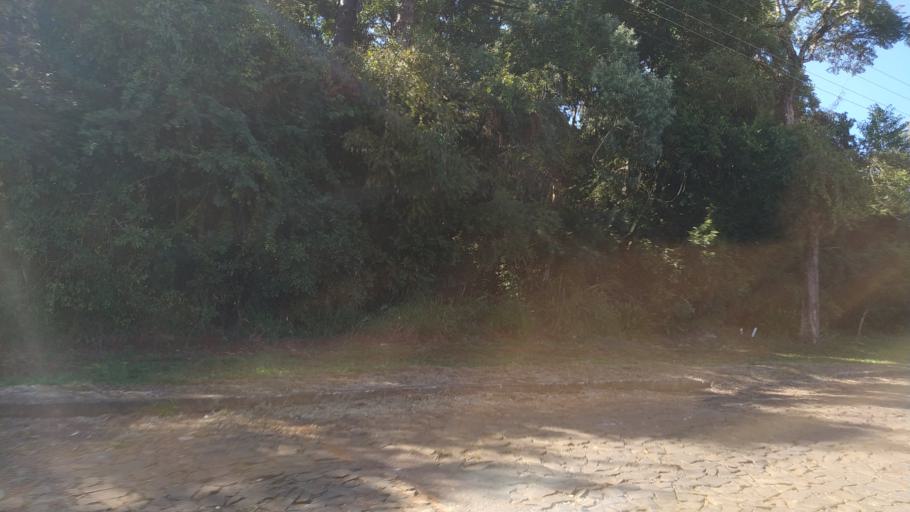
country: BR
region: Santa Catarina
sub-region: Chapeco
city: Chapeco
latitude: -27.0787
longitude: -52.6018
